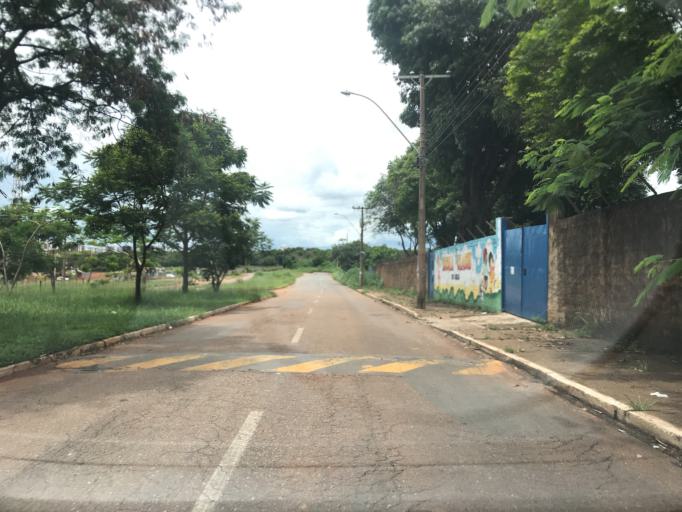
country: BR
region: Federal District
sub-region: Brasilia
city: Brasilia
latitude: -15.8137
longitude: -47.9586
